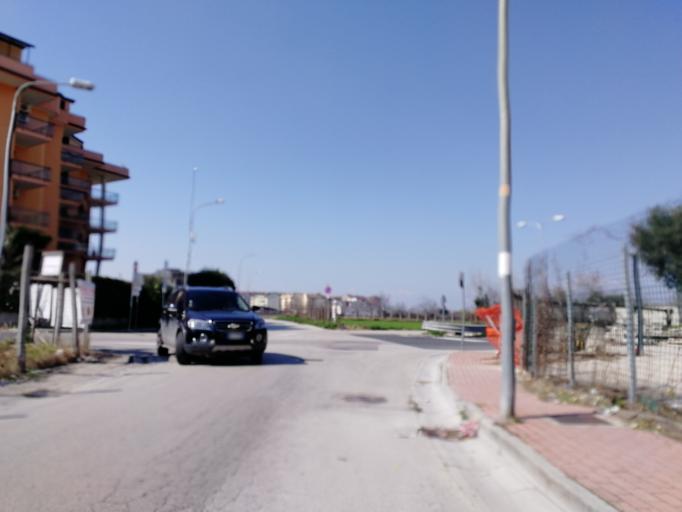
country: IT
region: Campania
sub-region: Provincia di Caserta
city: San Prisco
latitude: 41.0895
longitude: 14.2723
